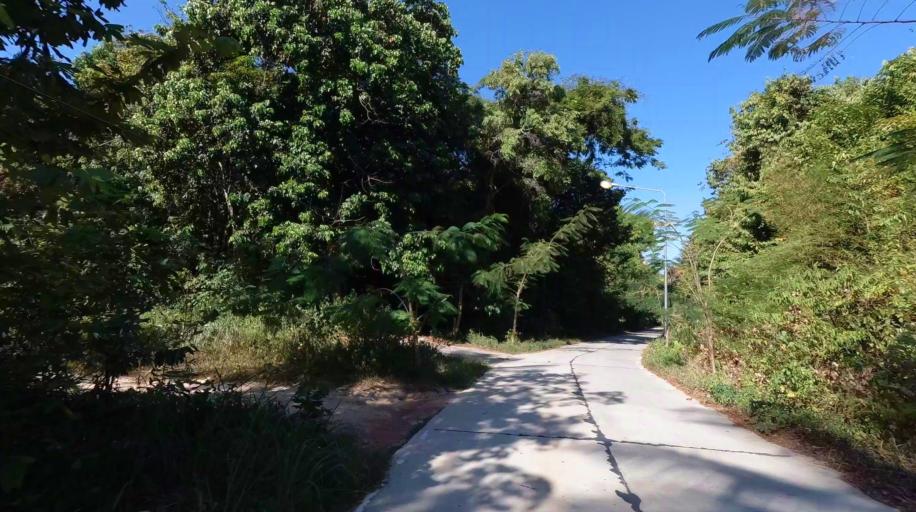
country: TH
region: Trat
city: Ko Kut
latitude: 11.6157
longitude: 102.5407
